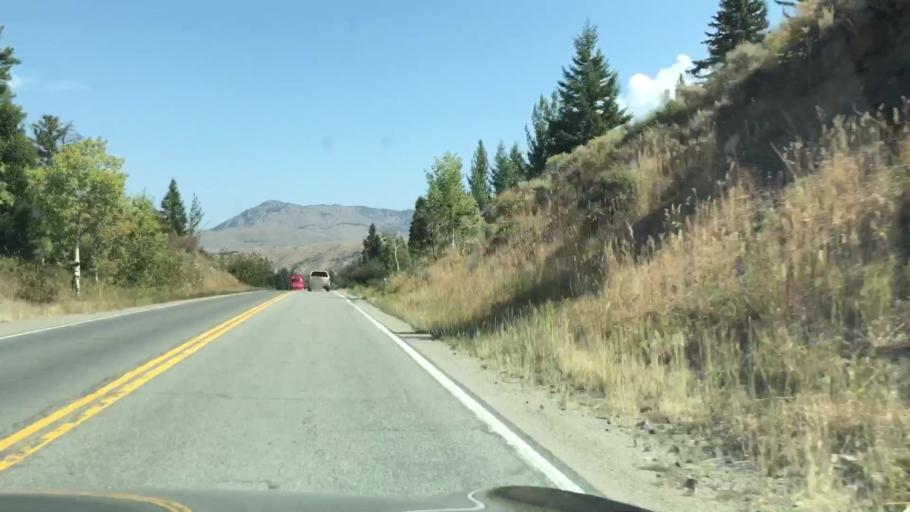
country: US
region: Wyoming
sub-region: Teton County
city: Hoback
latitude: 43.3316
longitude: -110.7276
